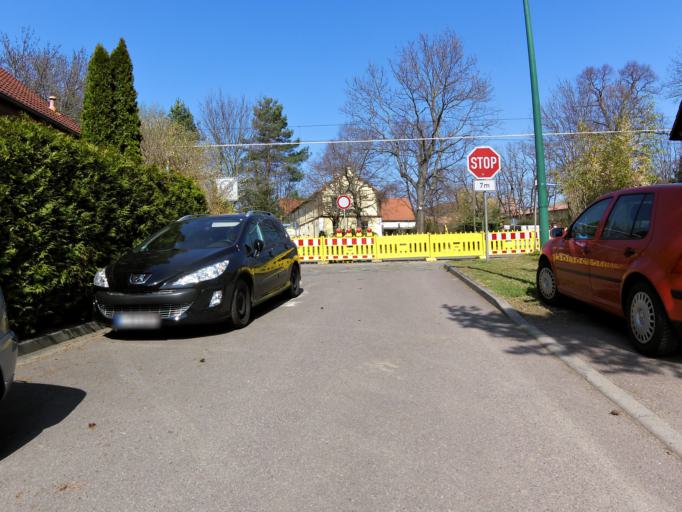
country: DE
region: Saxony
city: Leipzig
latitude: 51.3774
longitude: 12.3080
